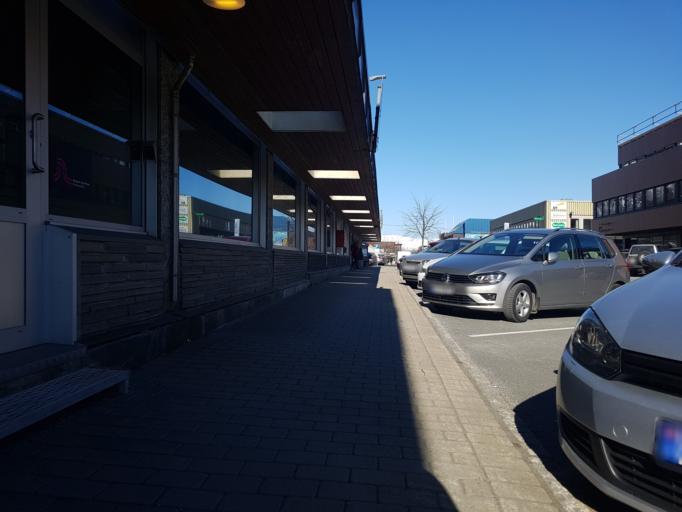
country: NO
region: Nordland
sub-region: Vefsn
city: Mosjoen
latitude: 65.8363
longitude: 13.1901
